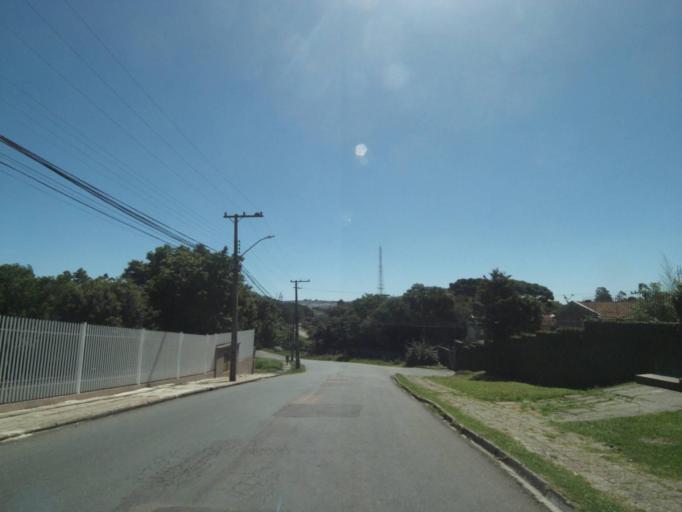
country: BR
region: Parana
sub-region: Curitiba
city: Curitiba
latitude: -25.4712
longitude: -49.3446
